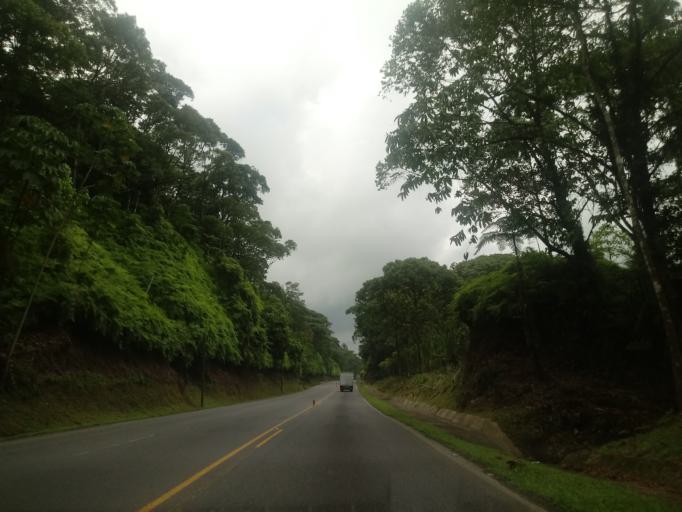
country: CR
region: San Jose
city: Dulce Nombre de Jesus
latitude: 10.1760
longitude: -83.9290
